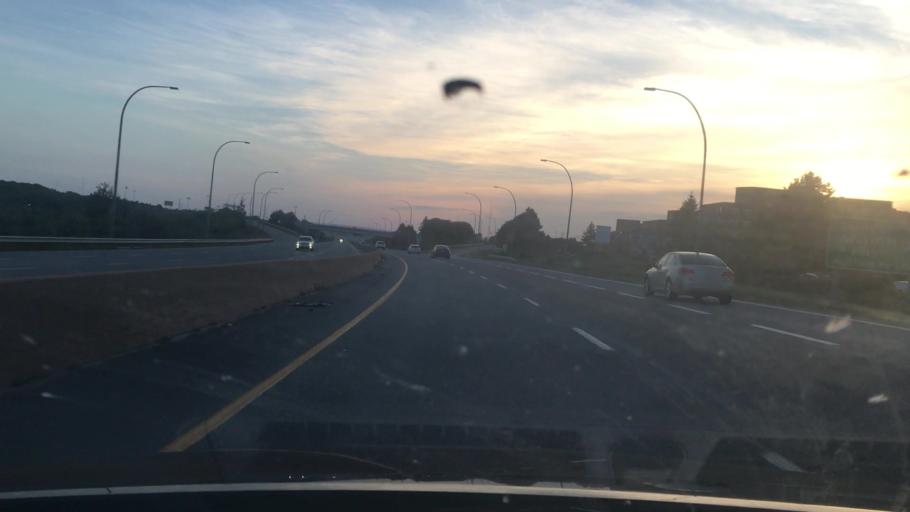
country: CA
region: Nova Scotia
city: Dartmouth
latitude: 44.6939
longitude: -63.5757
